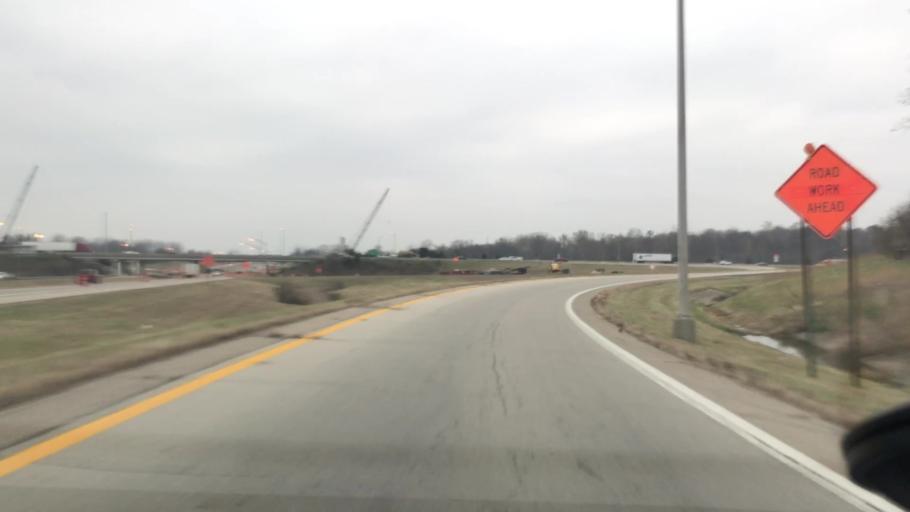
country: US
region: Ohio
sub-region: Clark County
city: Springfield
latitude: 39.8924
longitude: -83.8534
